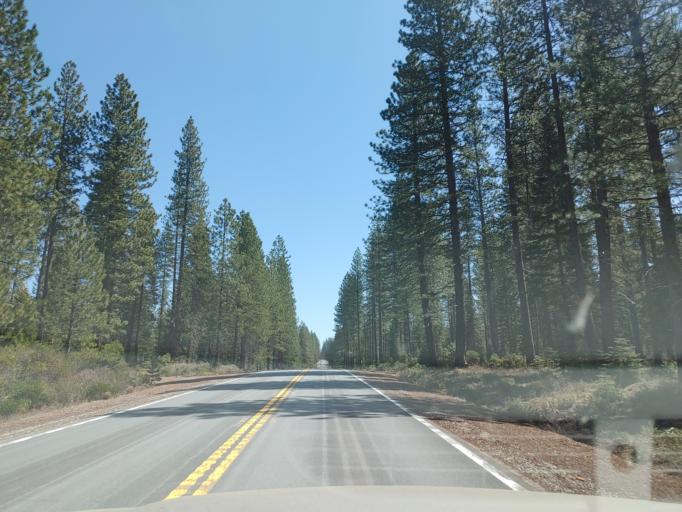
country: US
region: California
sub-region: Siskiyou County
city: McCloud
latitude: 41.2670
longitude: -121.8982
